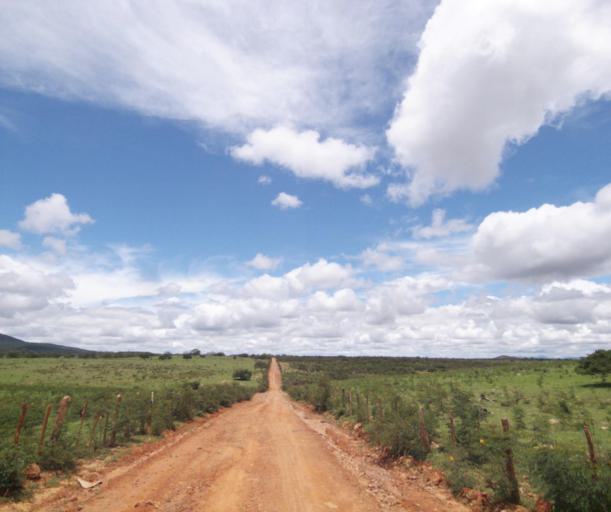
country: BR
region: Bahia
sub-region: Tanhacu
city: Tanhacu
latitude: -14.1909
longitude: -41.0673
